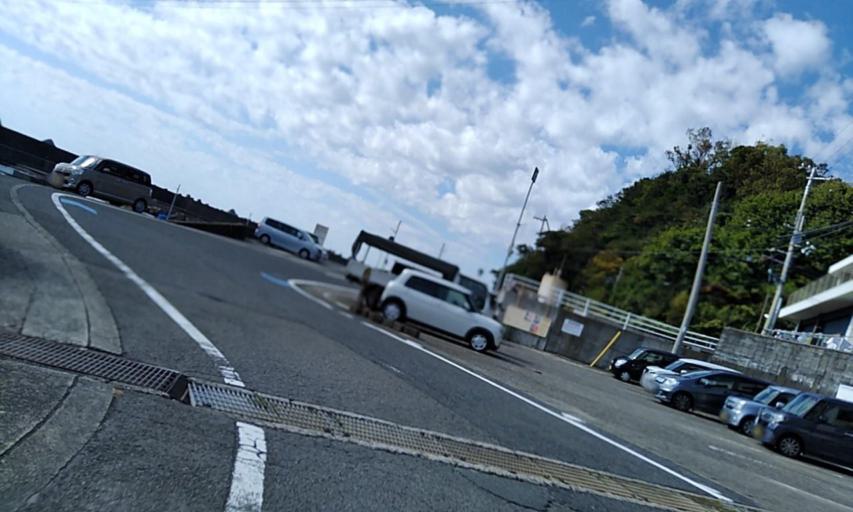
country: JP
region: Wakayama
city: Gobo
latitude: 33.9702
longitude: 135.0843
